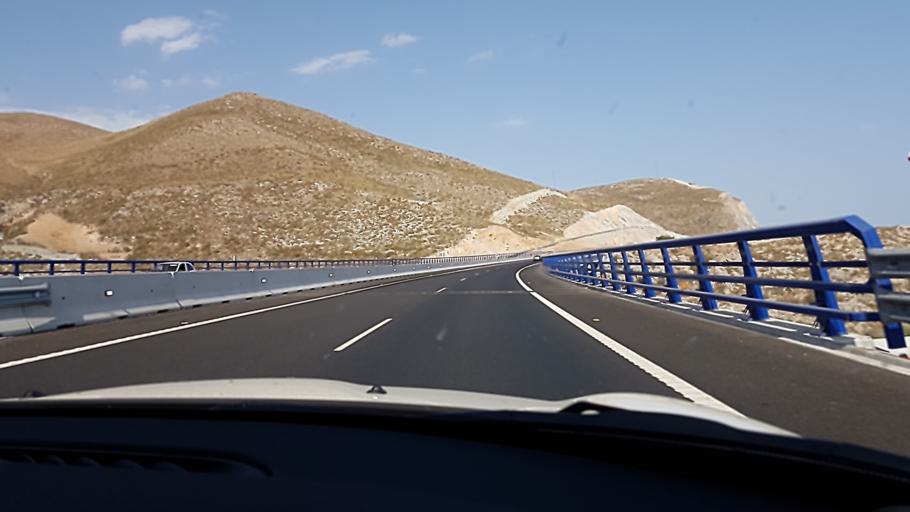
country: ES
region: Andalusia
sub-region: Provincia de Granada
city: Gualchos
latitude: 36.7145
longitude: -3.3970
